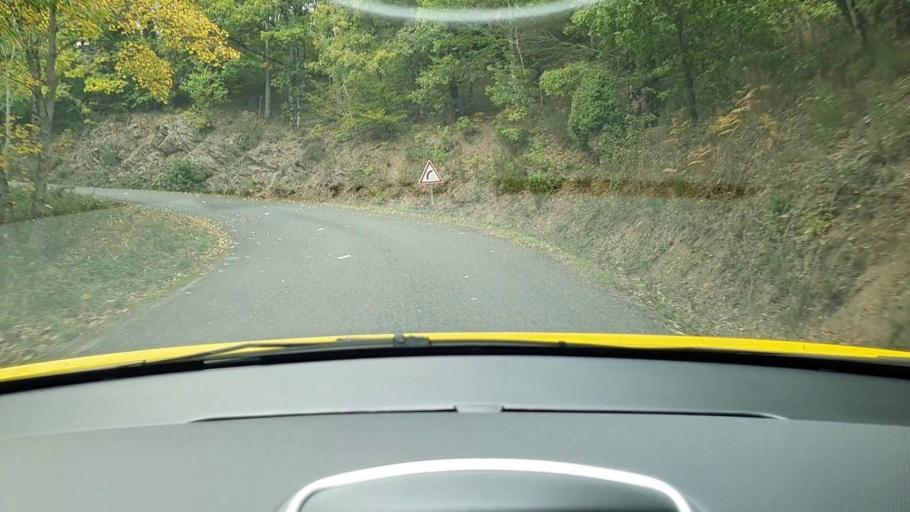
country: FR
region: Languedoc-Roussillon
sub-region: Departement de la Lozere
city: Meyrueis
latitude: 44.0798
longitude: 3.4152
